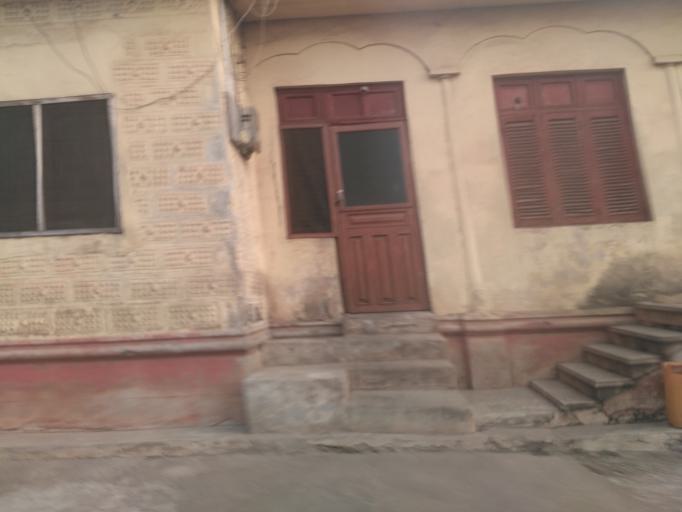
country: GH
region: Ashanti
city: Kumasi
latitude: 6.7050
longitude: -1.6177
